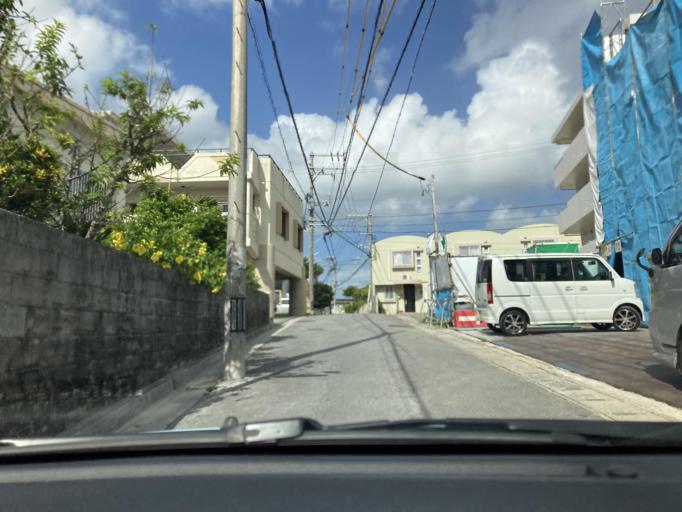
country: JP
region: Okinawa
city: Naha-shi
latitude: 26.2035
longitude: 127.7093
